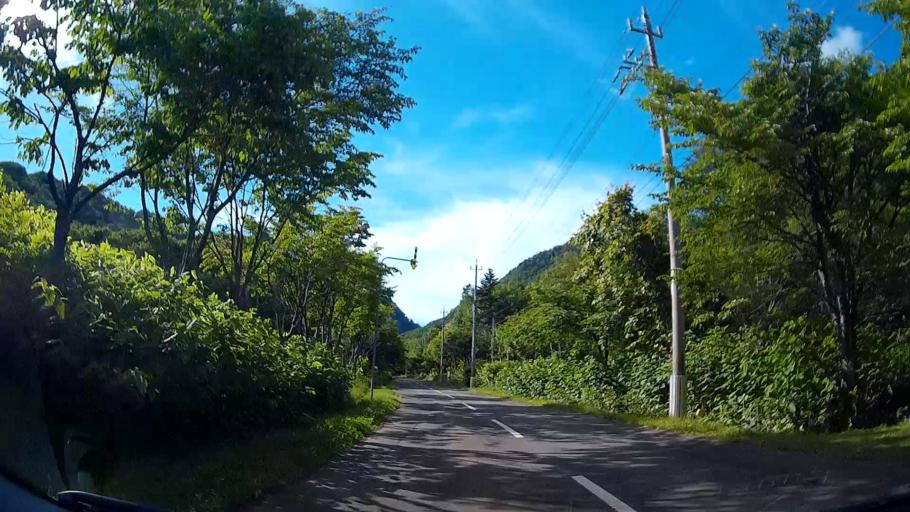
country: JP
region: Hokkaido
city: Sapporo
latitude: 42.9749
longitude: 141.1656
